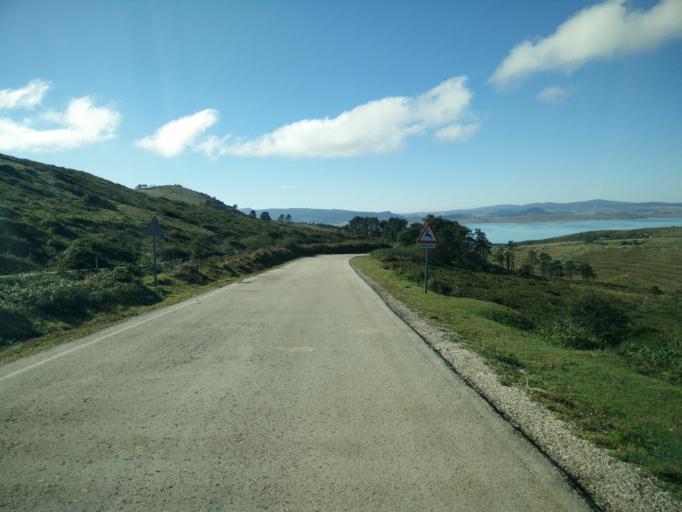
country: ES
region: Cantabria
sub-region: Provincia de Cantabria
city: San Pedro del Romeral
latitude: 43.0424
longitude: -3.8595
